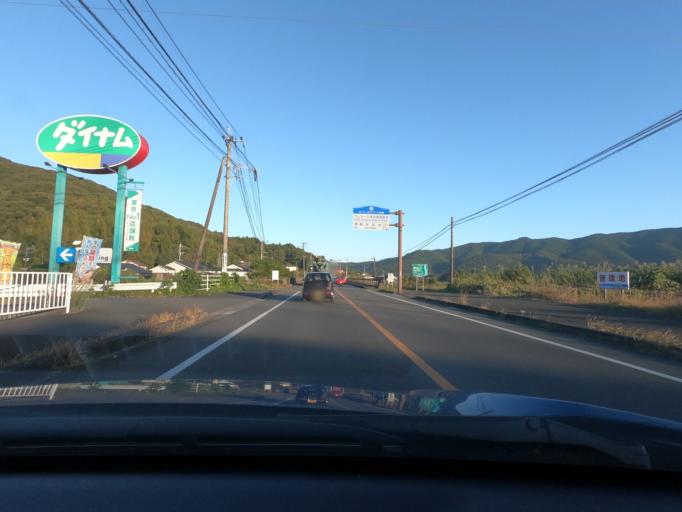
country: JP
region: Kagoshima
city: Satsumasendai
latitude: 31.8077
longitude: 130.3395
